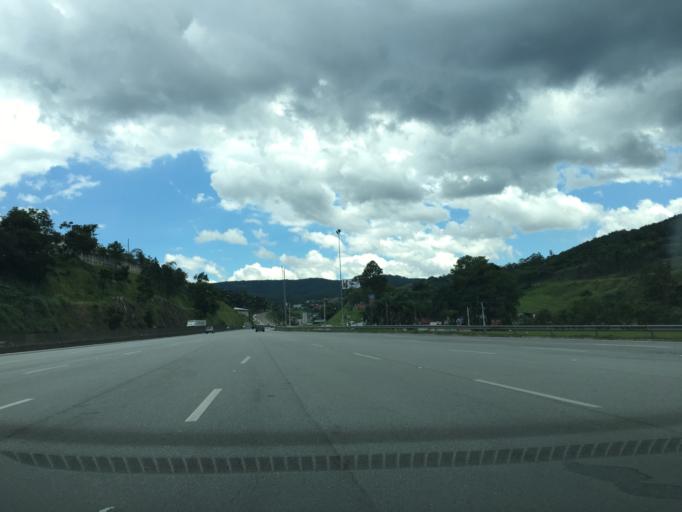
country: BR
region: Sao Paulo
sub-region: Mairipora
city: Mairipora
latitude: -23.3317
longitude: -46.5773
